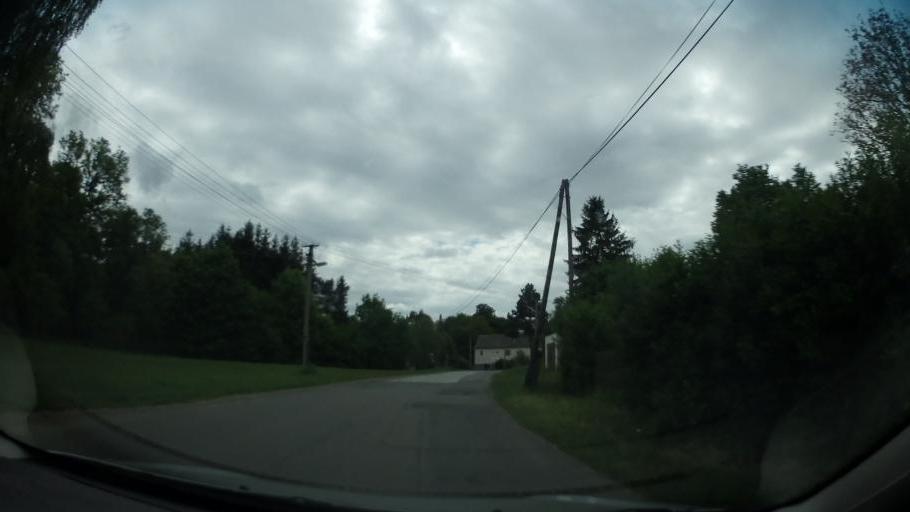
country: CZ
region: Pardubicky
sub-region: Okres Svitavy
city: Moravska Trebova
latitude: 49.8264
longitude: 16.7030
